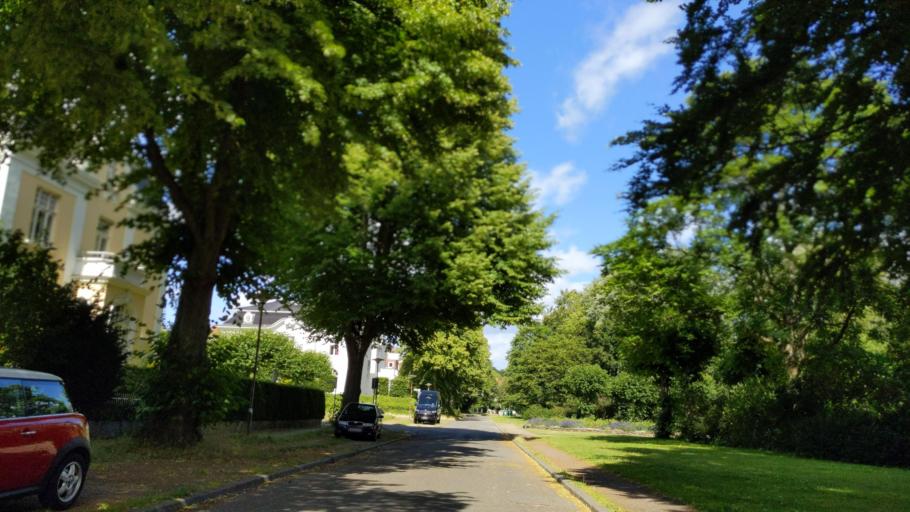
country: DE
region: Schleswig-Holstein
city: Luebeck
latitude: 53.8803
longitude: 10.7006
